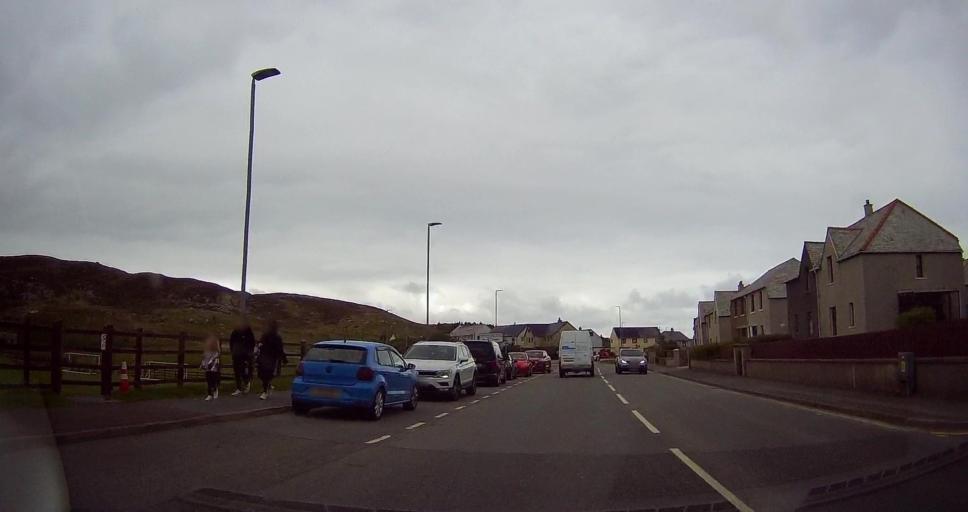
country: GB
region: Scotland
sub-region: Shetland Islands
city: Lerwick
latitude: 60.1554
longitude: -1.1595
